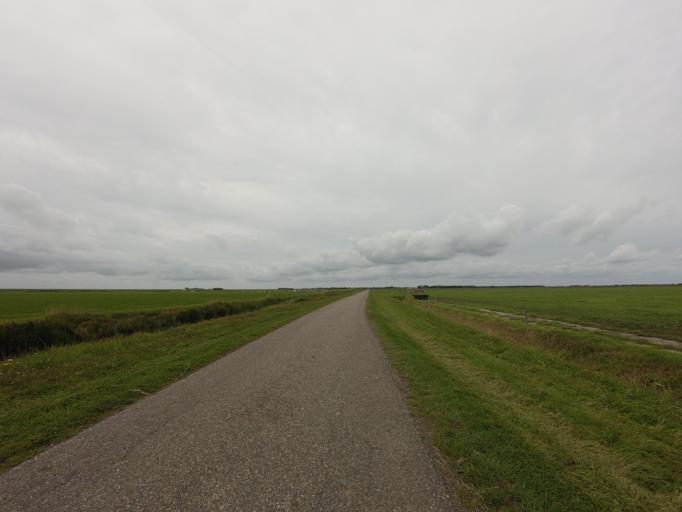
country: NL
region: Friesland
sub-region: Gemeente Ameland
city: Hollum
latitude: 53.4316
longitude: 5.6892
